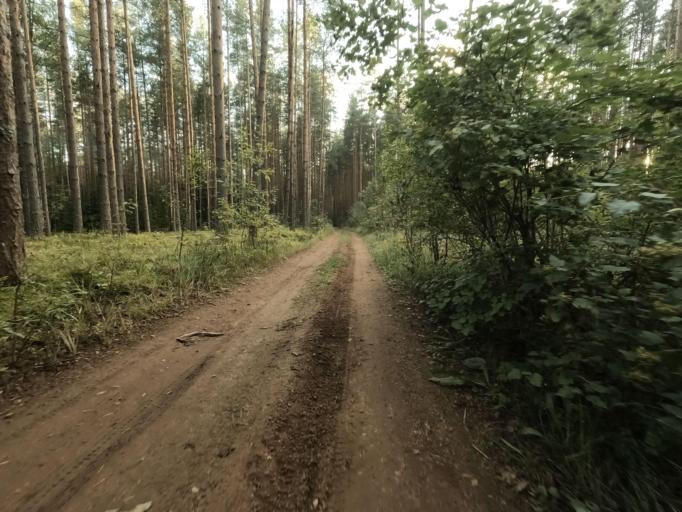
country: RU
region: Leningrad
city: Otradnoye
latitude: 59.8353
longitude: 30.7663
